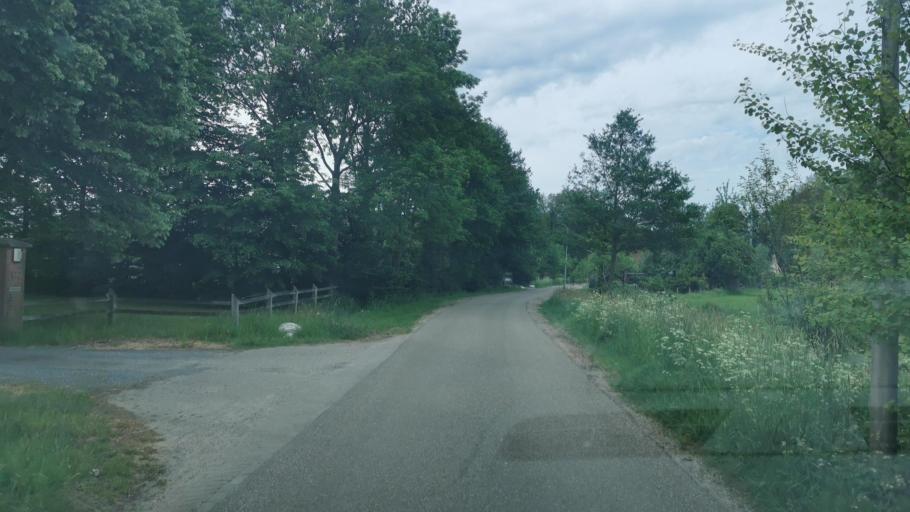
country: NL
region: Overijssel
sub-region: Gemeente Enschede
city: Enschede
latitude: 52.2570
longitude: 6.9102
